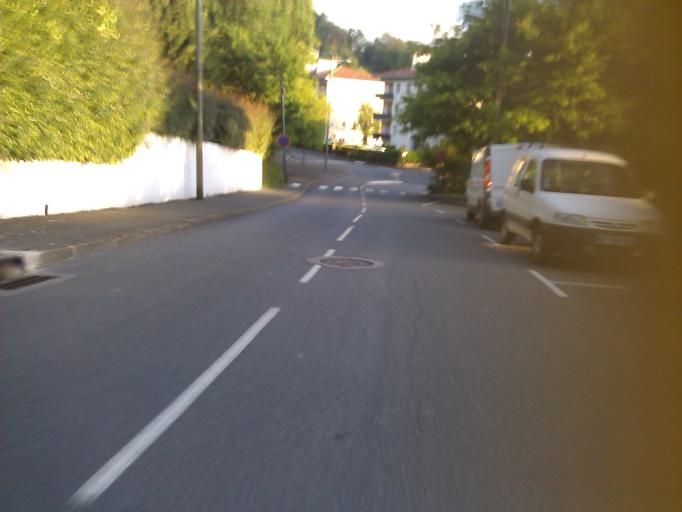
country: FR
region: Aquitaine
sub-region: Departement des Pyrenees-Atlantiques
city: Hendaye
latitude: 43.3668
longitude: -1.7696
